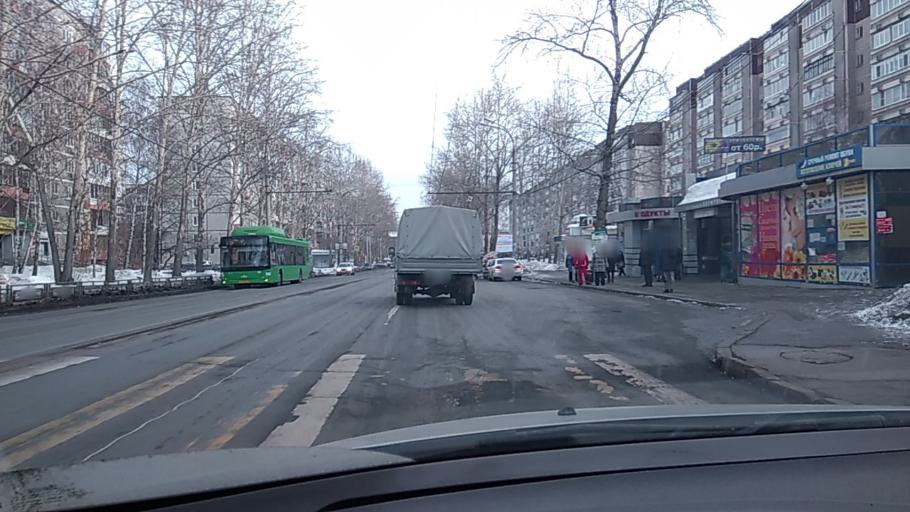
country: RU
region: Sverdlovsk
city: Sovkhoznyy
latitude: 56.7929
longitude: 60.5746
